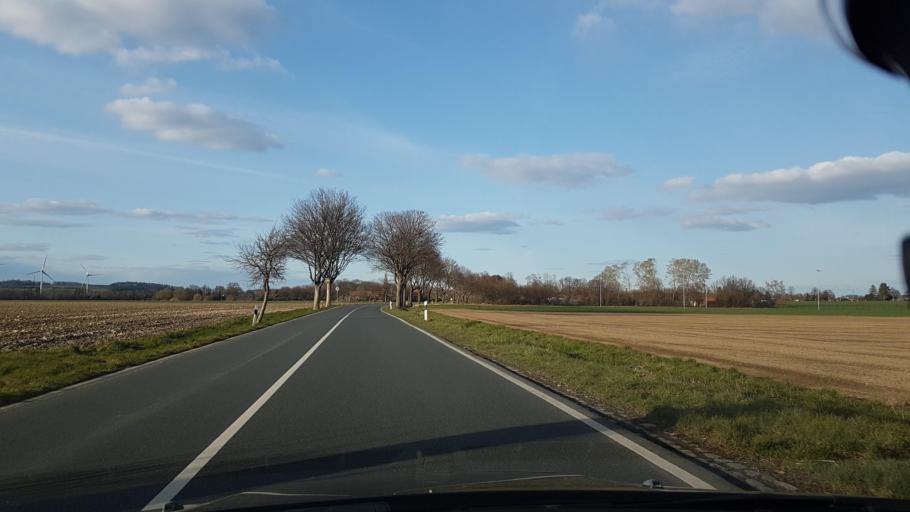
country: DE
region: Lower Saxony
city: Egestorf
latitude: 52.3106
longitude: 9.5456
